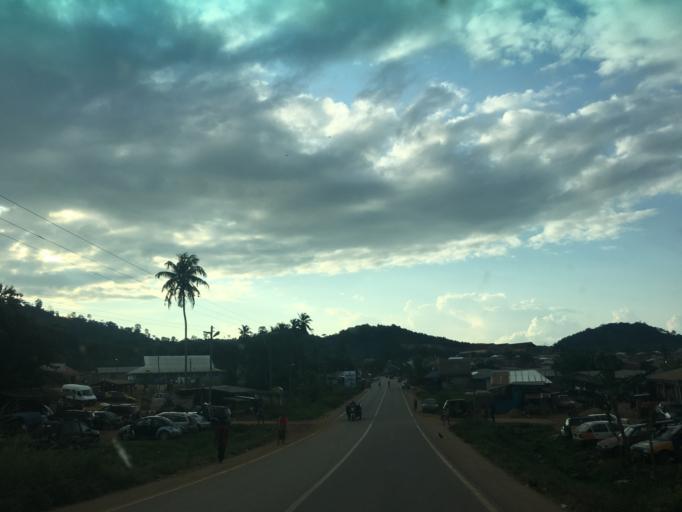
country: GH
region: Western
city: Bibiani
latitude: 6.4603
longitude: -2.3209
